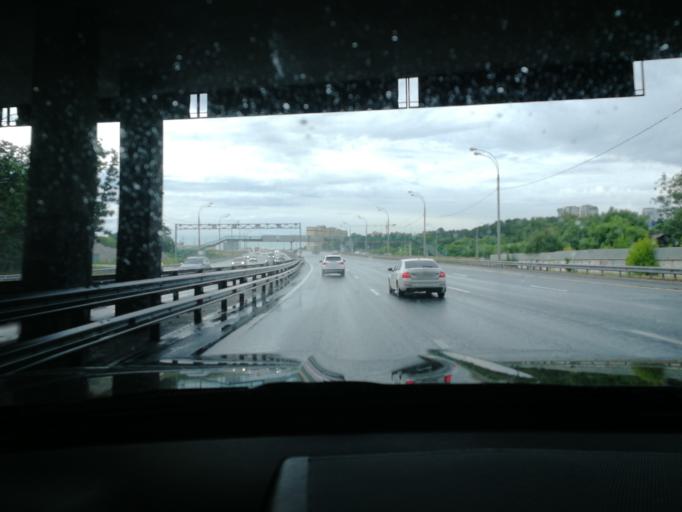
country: RU
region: Moskovskaya
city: Vidnoye
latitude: 55.5435
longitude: 37.6956
